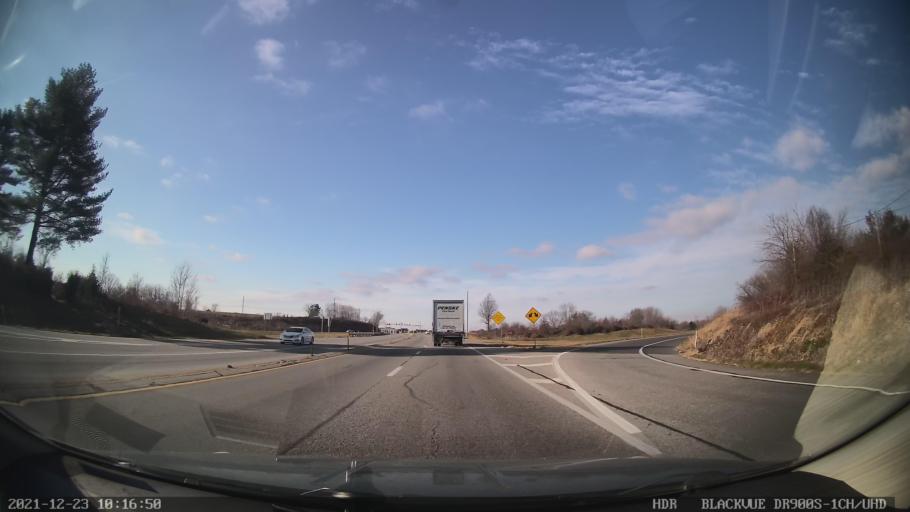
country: US
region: Pennsylvania
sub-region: Adams County
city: Lake Heritage
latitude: 39.8466
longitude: -77.1937
